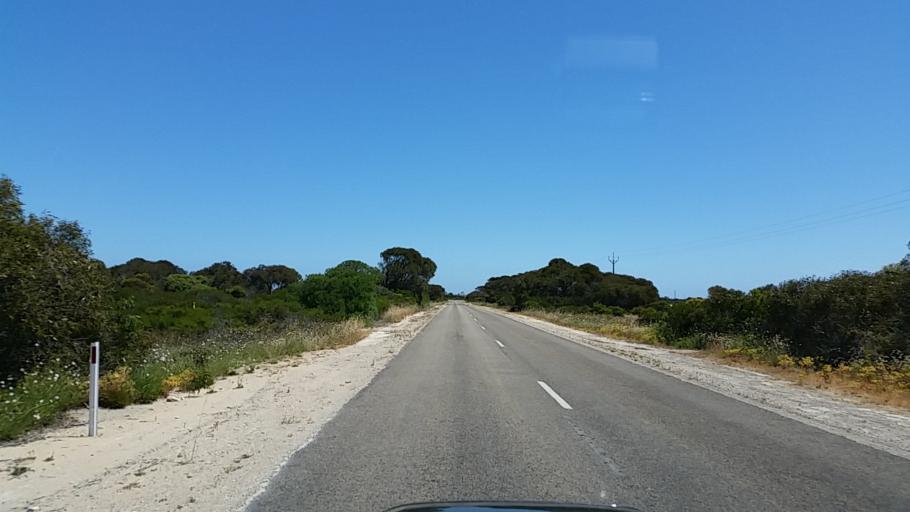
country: AU
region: South Australia
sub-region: Yorke Peninsula
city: Honiton
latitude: -35.2191
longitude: 136.9991
